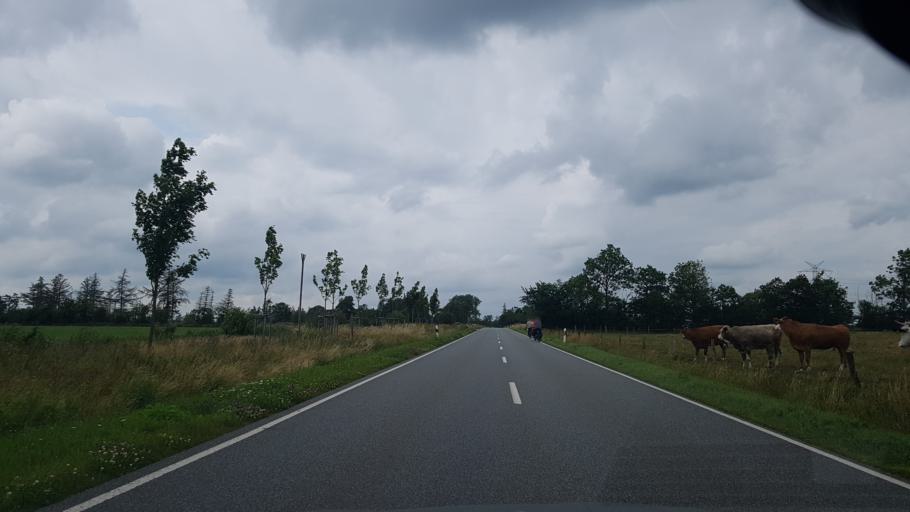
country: DE
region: Schleswig-Holstein
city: Osterby
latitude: 54.8139
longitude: 9.2299
